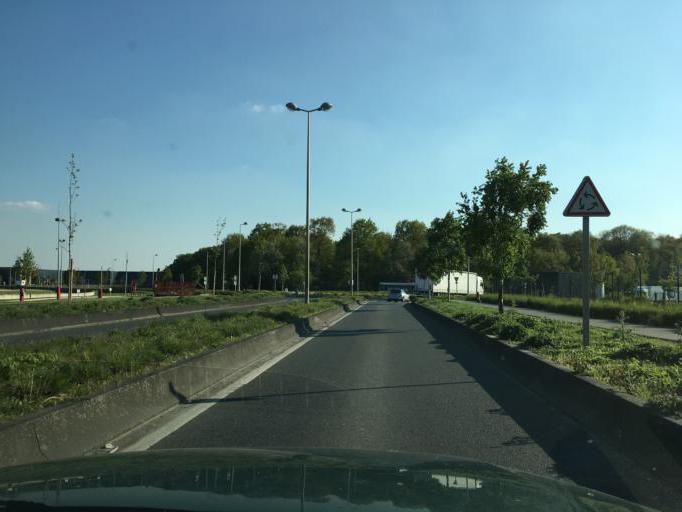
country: FR
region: Centre
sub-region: Departement du Loiret
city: Gidy
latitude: 47.9603
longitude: 1.8463
